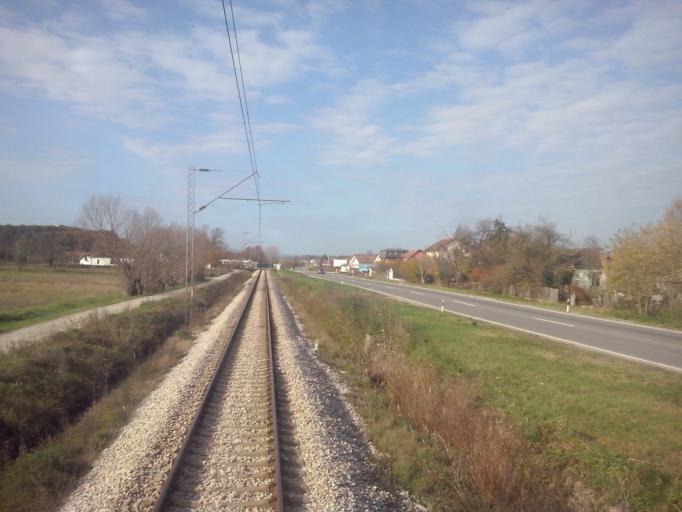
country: RS
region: Central Serbia
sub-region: Kolubarski Okrug
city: Valjevo
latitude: 44.2944
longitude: 19.9862
